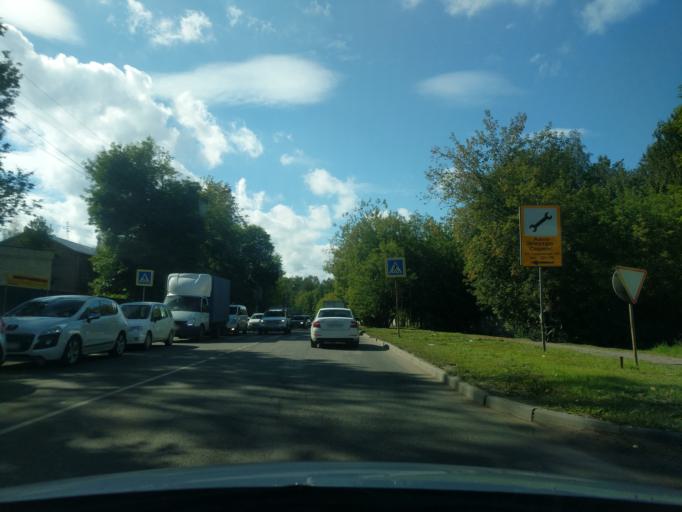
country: RU
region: Kostroma
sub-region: Kostromskoy Rayon
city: Kostroma
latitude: 57.7796
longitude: 40.9631
